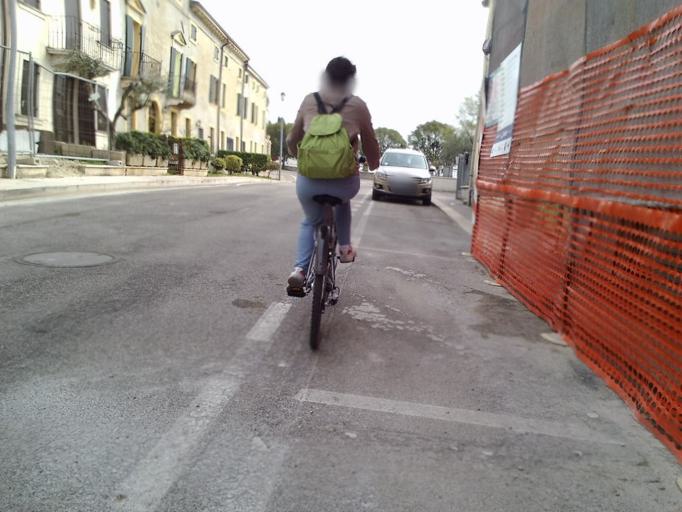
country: IT
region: Veneto
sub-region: Provincia di Verona
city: Rosegaferro
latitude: 45.3722
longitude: 10.7940
